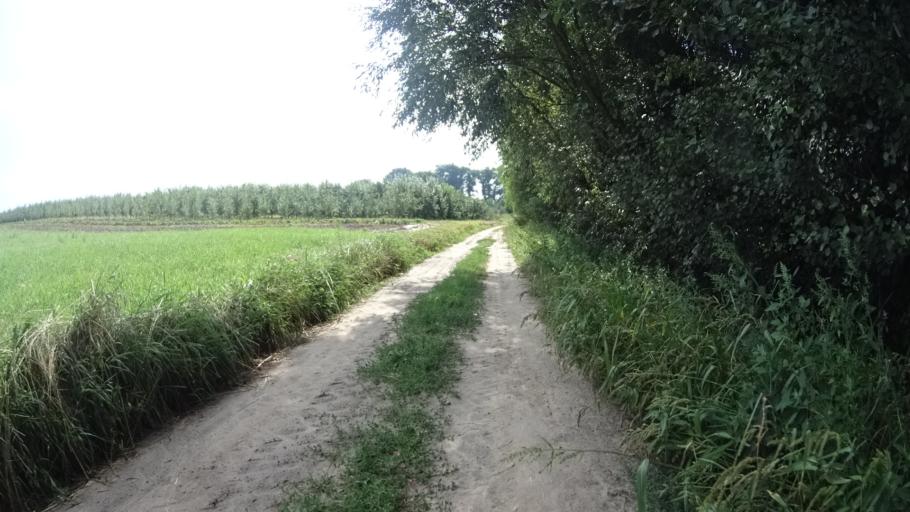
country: PL
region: Masovian Voivodeship
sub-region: Powiat grojecki
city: Goszczyn
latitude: 51.7001
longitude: 20.8516
